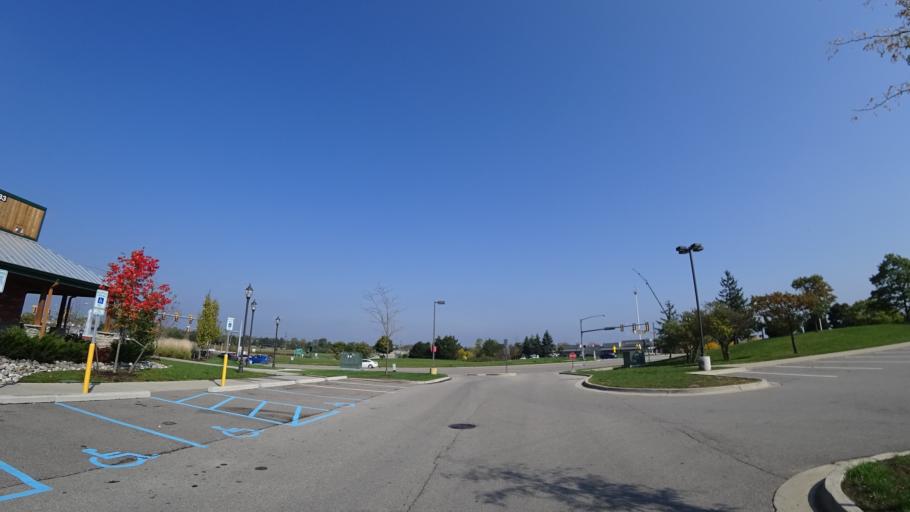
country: US
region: Michigan
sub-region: Washtenaw County
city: Ann Arbor
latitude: 42.2415
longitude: -83.7673
